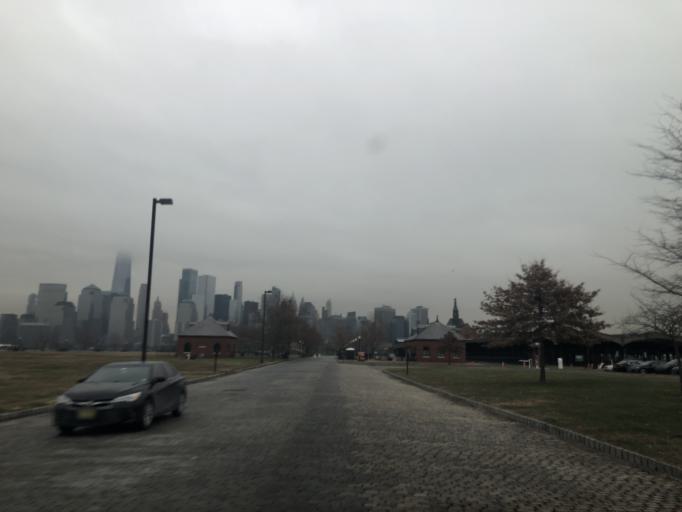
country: US
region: New York
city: New York City
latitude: 40.7085
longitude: -74.0395
